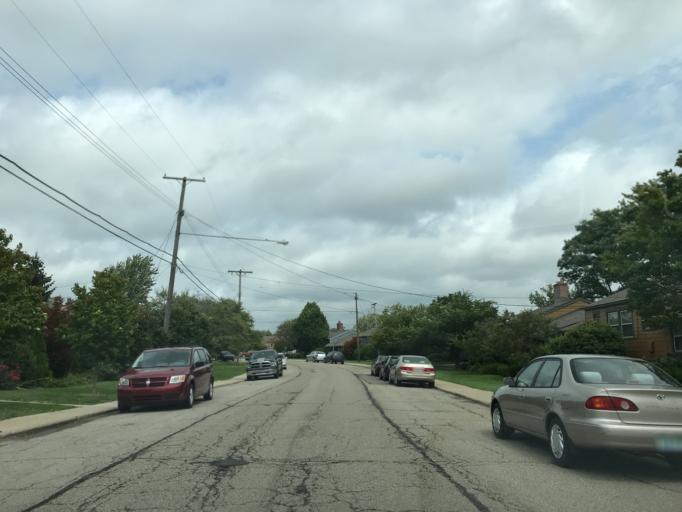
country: US
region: Michigan
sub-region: Washtenaw County
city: Ann Arbor
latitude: 42.2461
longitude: -83.6924
